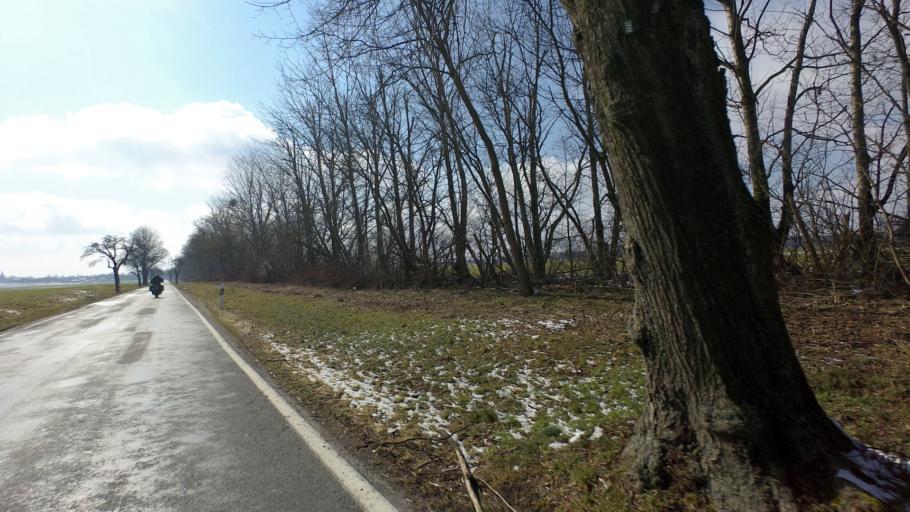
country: DE
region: Brandenburg
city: Werneuchen
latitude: 52.6945
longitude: 13.7239
